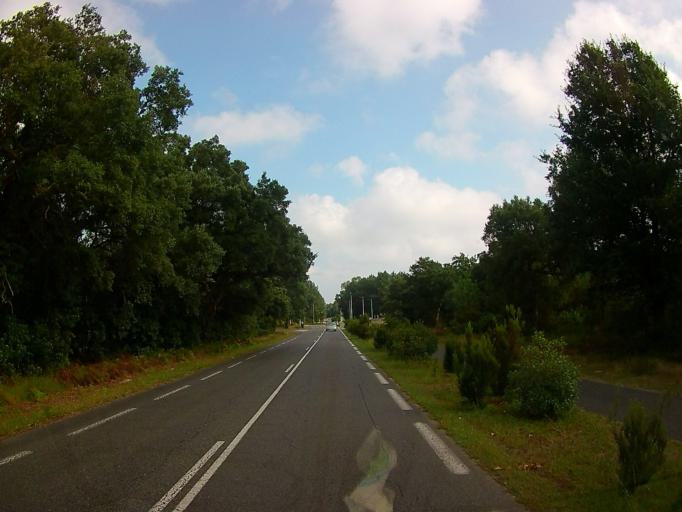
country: FR
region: Aquitaine
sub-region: Departement des Landes
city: Labenne
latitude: 43.5923
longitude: -1.4491
